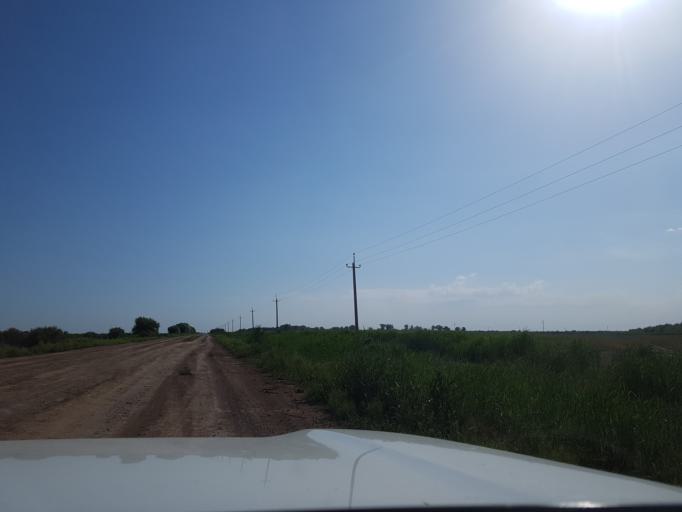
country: TM
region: Dasoguz
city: Koeneuergench
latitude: 42.0406
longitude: 58.8164
